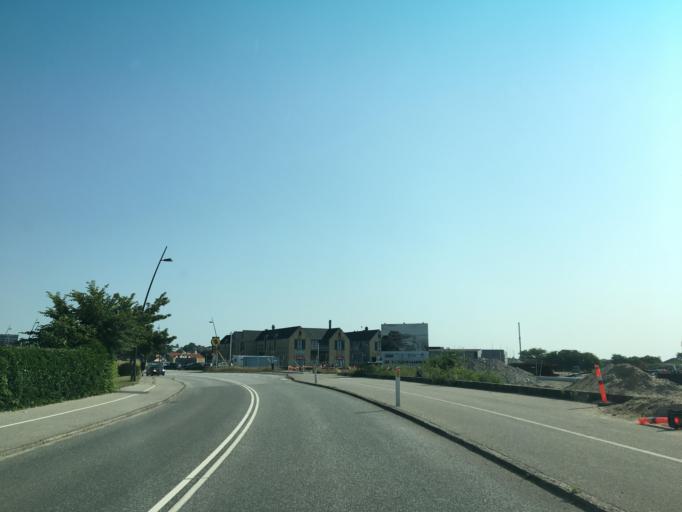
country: DK
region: North Denmark
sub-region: Thisted Kommune
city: Thisted
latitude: 56.9509
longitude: 8.6906
